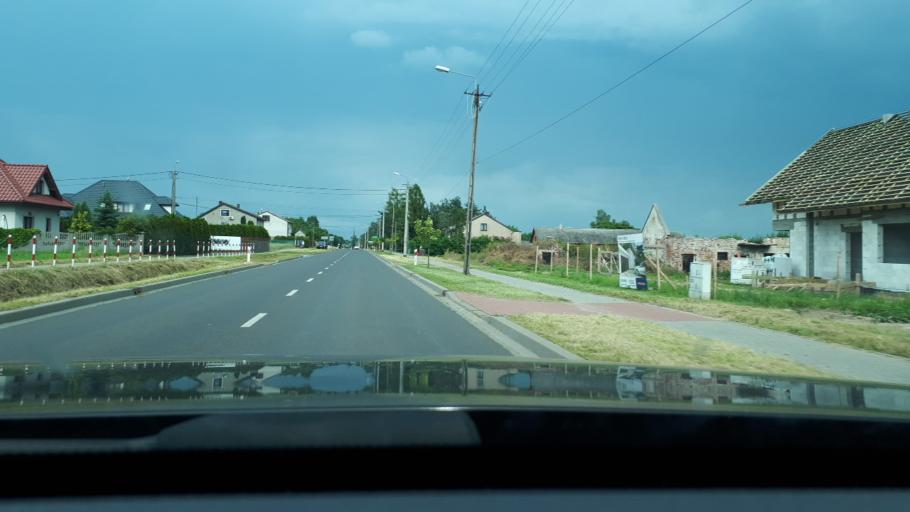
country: PL
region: Masovian Voivodeship
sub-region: Powiat warszawski zachodni
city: Leszno
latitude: 52.2576
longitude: 20.5512
